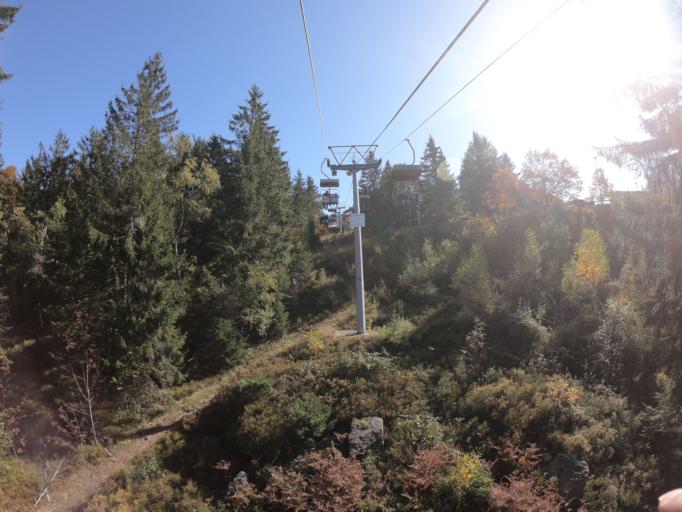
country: DE
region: Bavaria
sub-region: Lower Bavaria
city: Bodenmais
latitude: 49.0599
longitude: 13.1216
